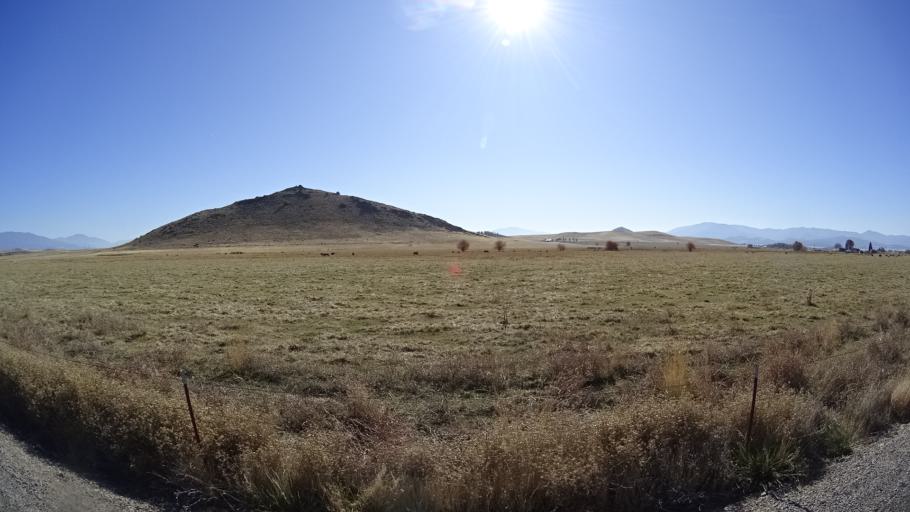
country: US
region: California
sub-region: Siskiyou County
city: Montague
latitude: 41.7566
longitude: -122.4910
